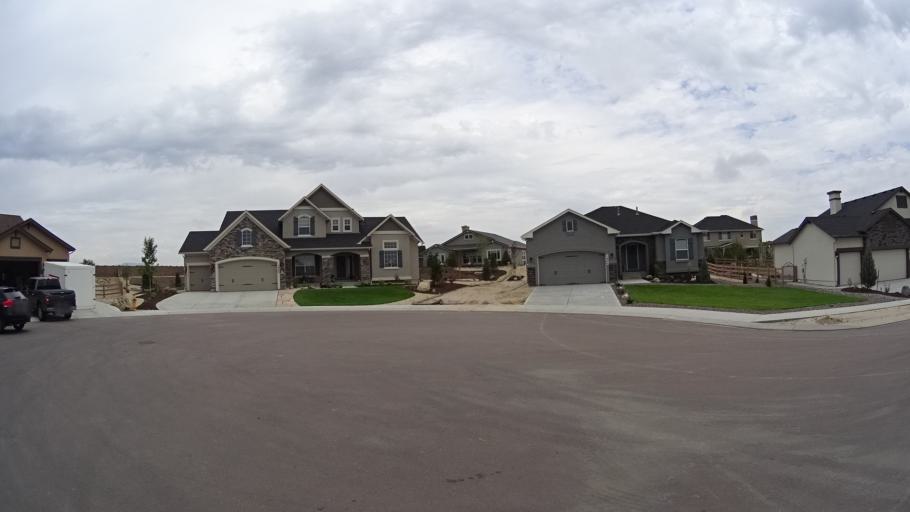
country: US
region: Colorado
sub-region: El Paso County
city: Gleneagle
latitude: 39.0059
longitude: -104.7929
